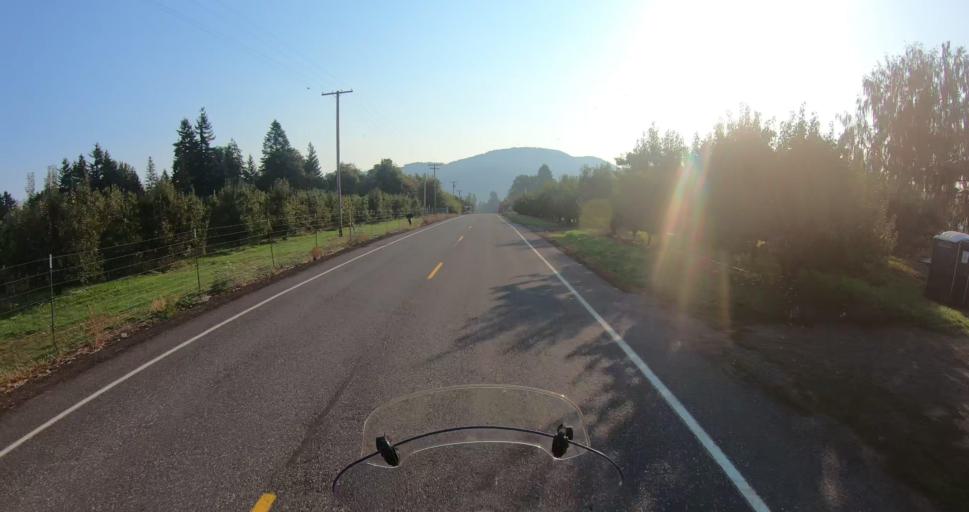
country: US
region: Oregon
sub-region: Hood River County
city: Odell
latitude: 45.5418
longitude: -121.5955
